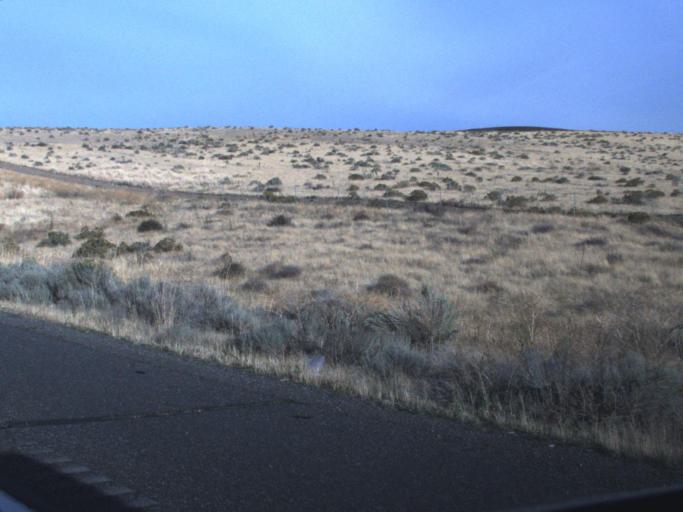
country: US
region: Oregon
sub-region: Umatilla County
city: Umatilla
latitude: 46.0015
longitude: -119.2539
